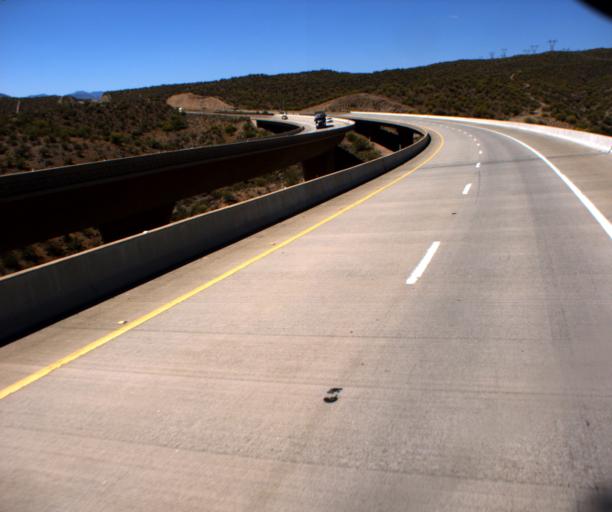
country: US
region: Arizona
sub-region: Yavapai County
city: Bagdad
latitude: 34.5773
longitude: -113.4902
